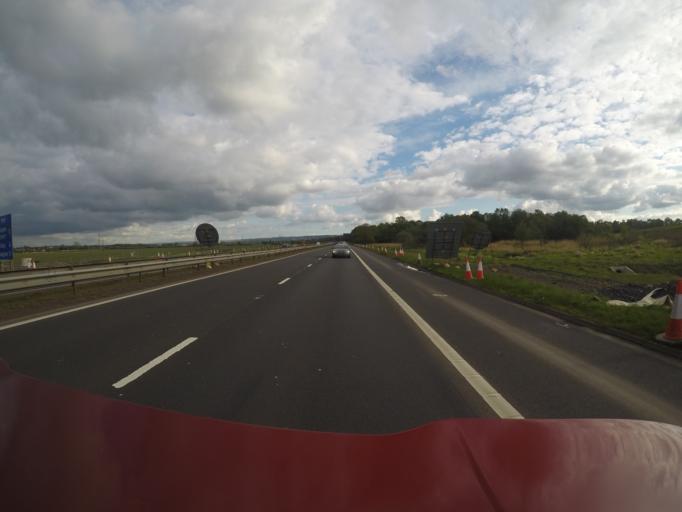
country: GB
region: Scotland
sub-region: Renfrewshire
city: Bishopton
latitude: 55.8895
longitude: -4.4807
